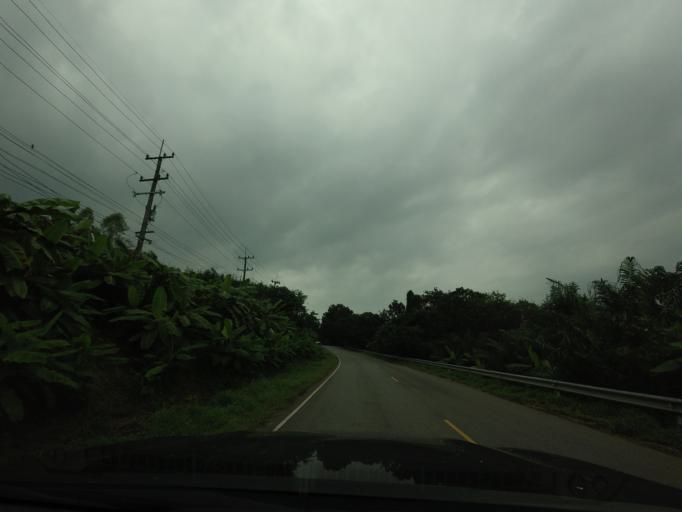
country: TH
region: Nong Khai
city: Sangkhom
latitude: 18.0457
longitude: 102.3288
